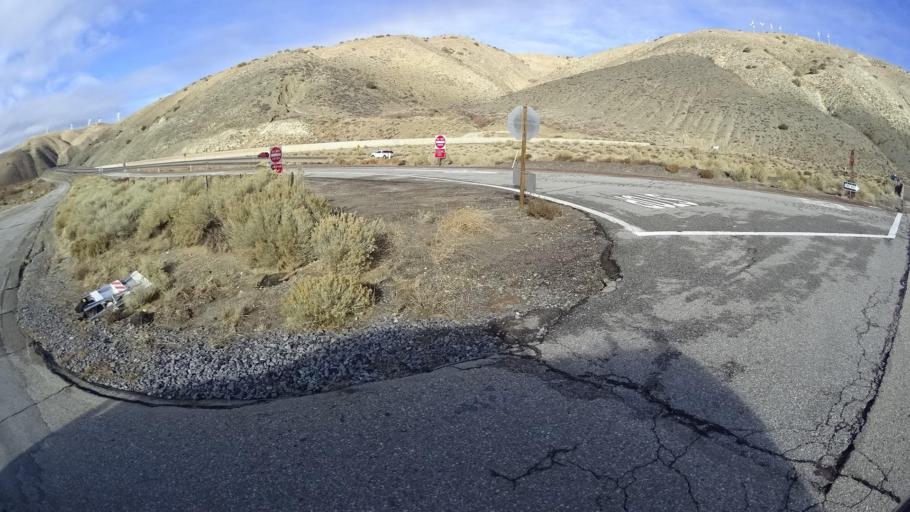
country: US
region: California
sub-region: Kern County
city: Mojave
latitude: 35.0986
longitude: -118.2931
